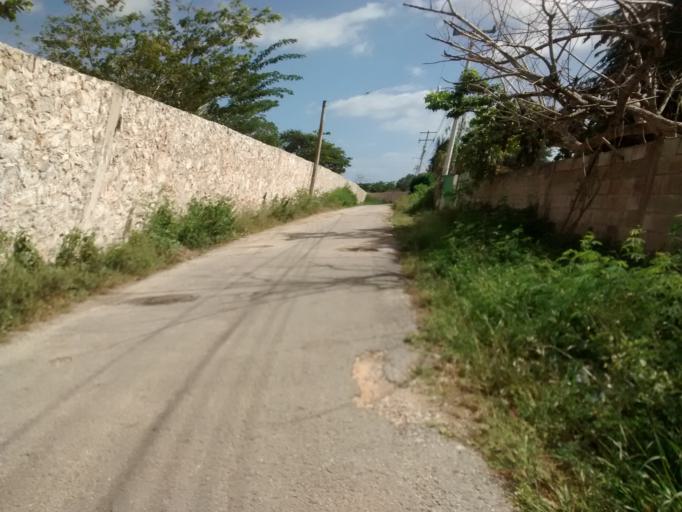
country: MX
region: Yucatan
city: Valladolid
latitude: 20.6838
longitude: -88.1874
